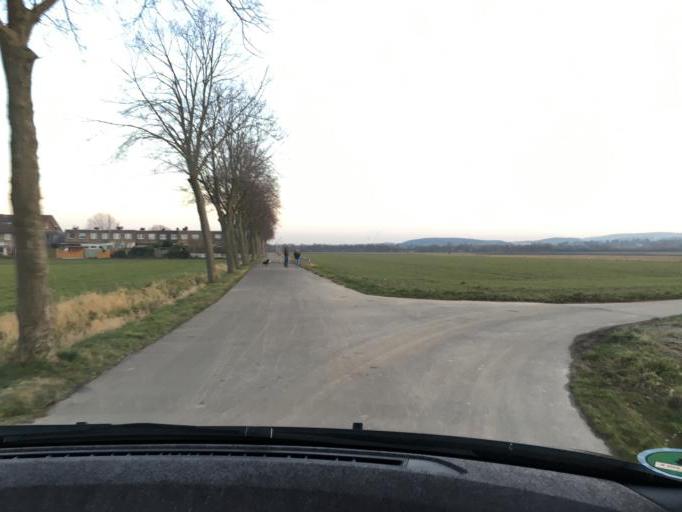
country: DE
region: North Rhine-Westphalia
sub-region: Regierungsbezirk Koln
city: Dueren
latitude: 50.7786
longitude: 6.4628
